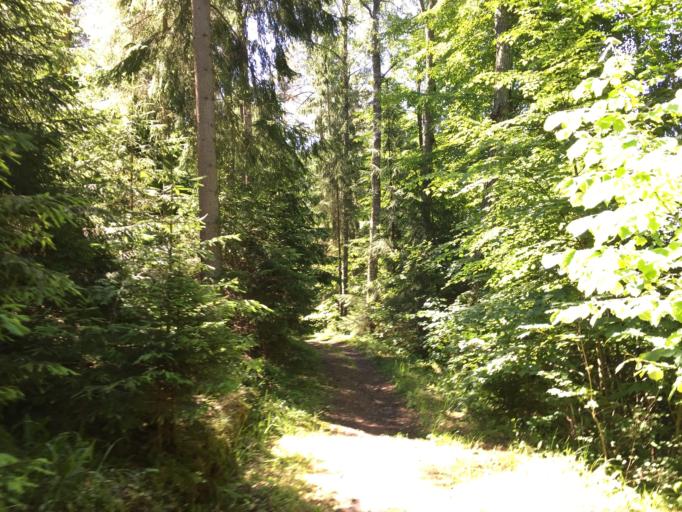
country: LV
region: Sigulda
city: Sigulda
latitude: 57.2226
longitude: 24.9086
